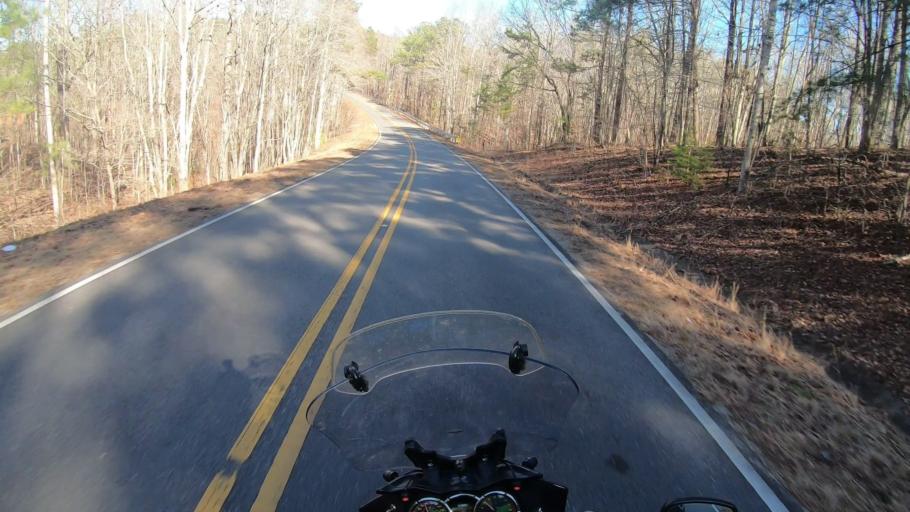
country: US
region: Alabama
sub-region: Calhoun County
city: Choccolocco
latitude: 33.5377
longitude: -85.7342
